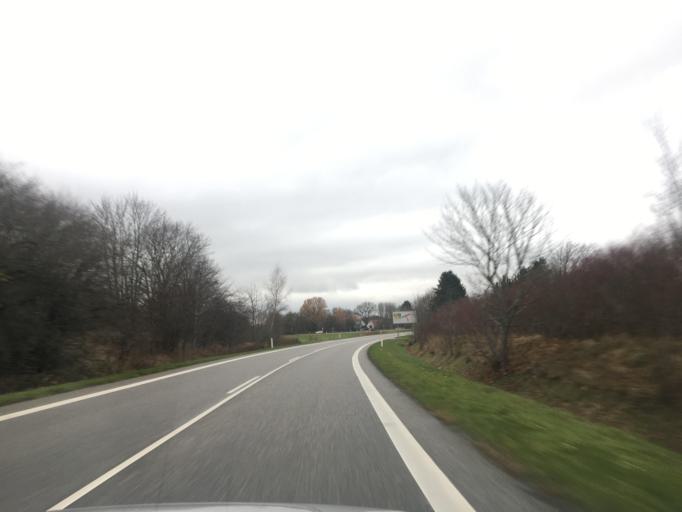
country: DK
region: Zealand
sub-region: Holbaek Kommune
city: Holbaek
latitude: 55.7208
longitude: 11.6402
